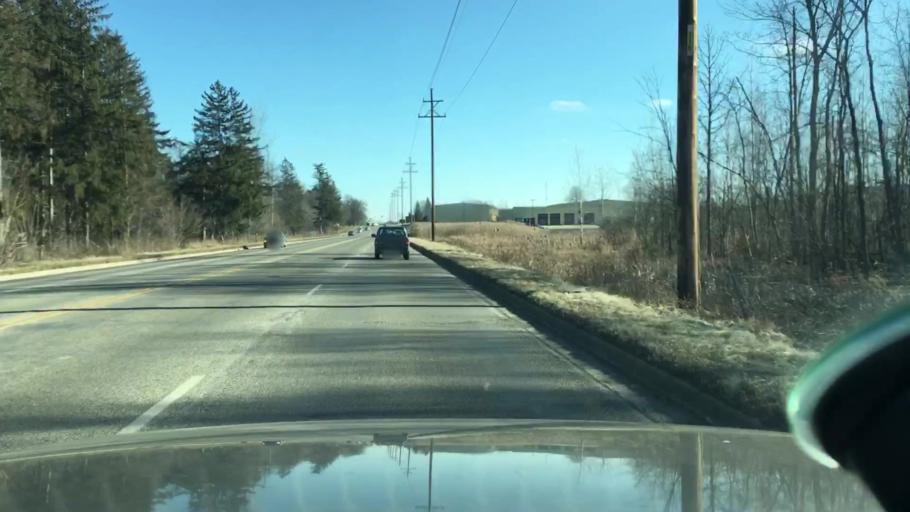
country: US
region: Michigan
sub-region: Jackson County
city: Jackson
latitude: 42.2911
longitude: -84.4039
